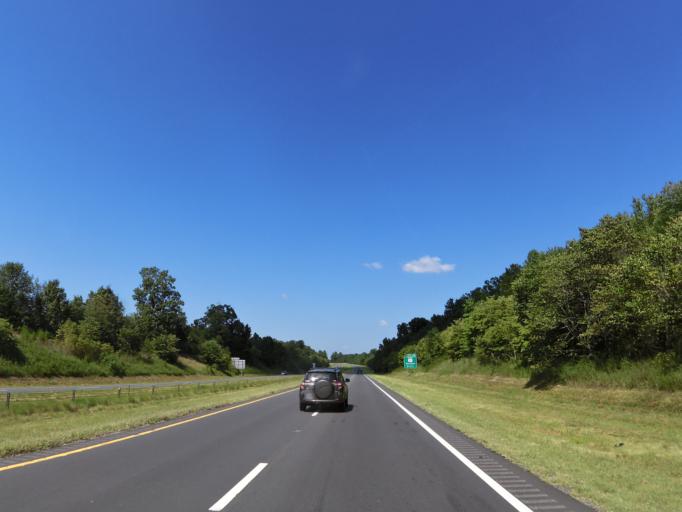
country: US
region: North Carolina
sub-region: Lincoln County
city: Lincolnton
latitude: 35.4934
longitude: -81.2294
